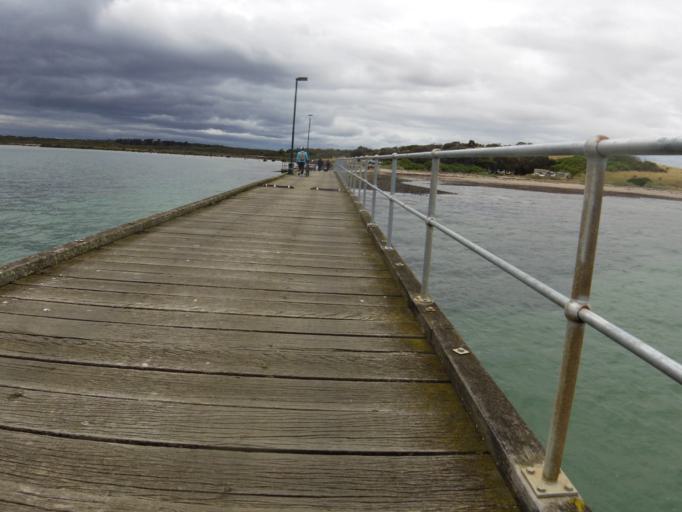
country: AU
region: Victoria
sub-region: Bass Coast
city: Cowes
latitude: -38.3831
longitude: 145.2709
